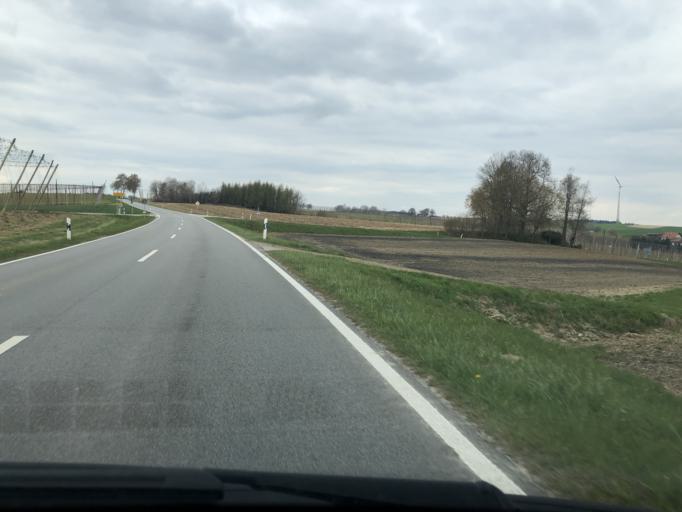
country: DE
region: Bavaria
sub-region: Upper Bavaria
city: Wolfersdorf
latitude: 48.5094
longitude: 11.6782
